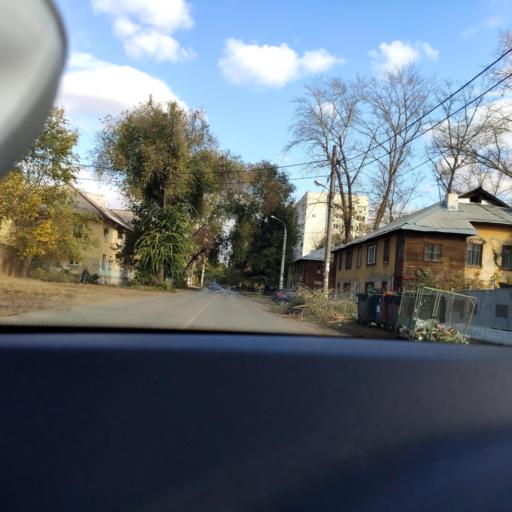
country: RU
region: Samara
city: Samara
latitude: 53.2305
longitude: 50.2636
